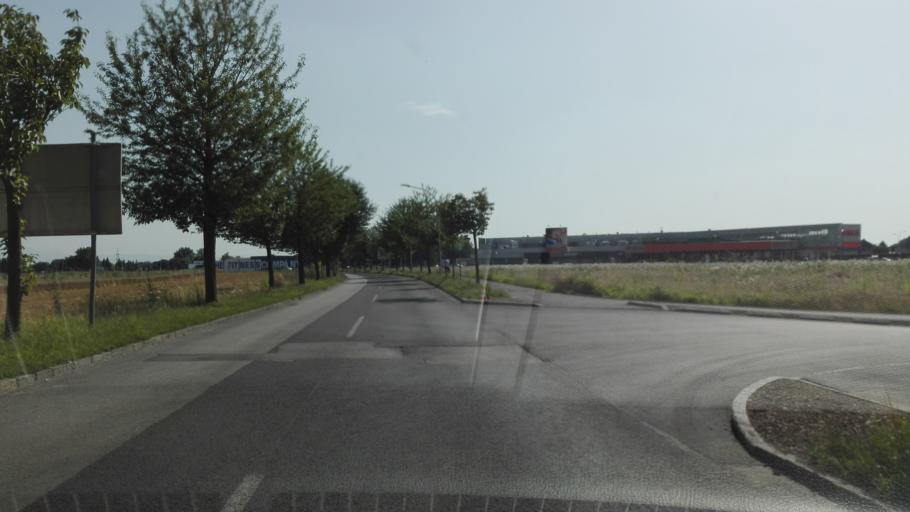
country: AT
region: Upper Austria
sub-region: Politischer Bezirk Linz-Land
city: Leonding
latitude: 48.2625
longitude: 14.2621
